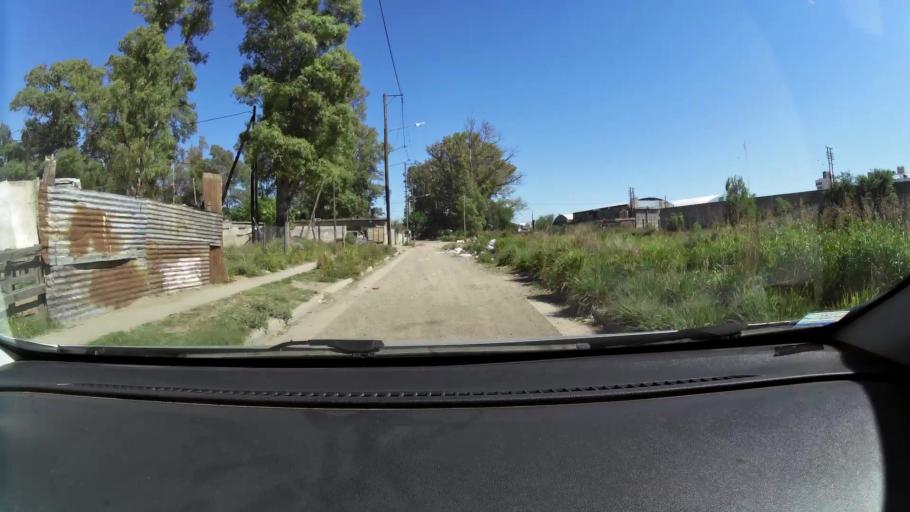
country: AR
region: Cordoba
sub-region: Departamento de Capital
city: Cordoba
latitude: -31.4374
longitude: -64.1322
